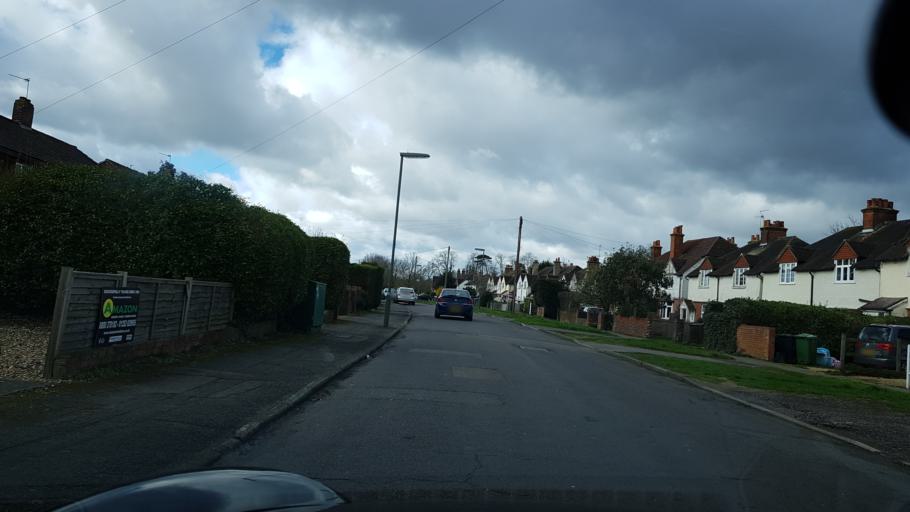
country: GB
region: England
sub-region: Surrey
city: Guildford
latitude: 51.2583
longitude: -0.5697
